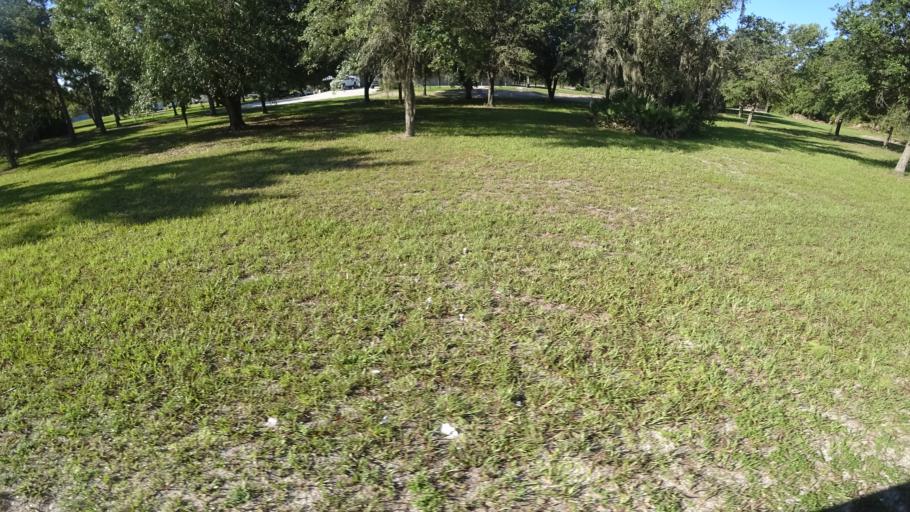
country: US
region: Florida
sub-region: Sarasota County
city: The Meadows
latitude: 27.4194
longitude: -82.2630
